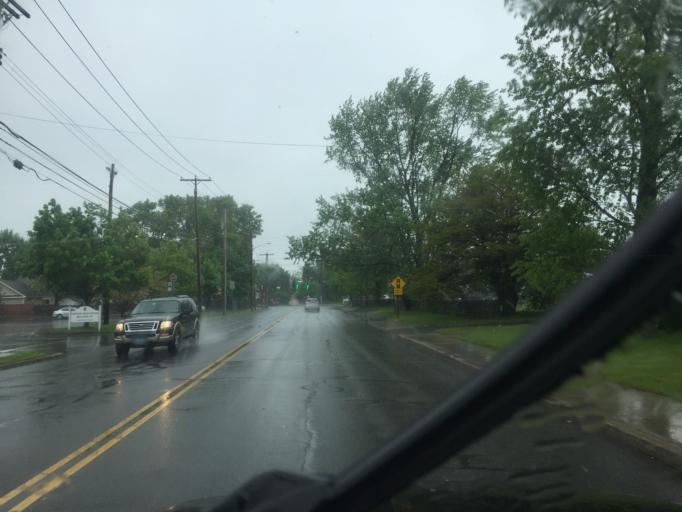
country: US
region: Connecticut
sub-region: Fairfield County
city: Fairfield
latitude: 41.1434
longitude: -73.2650
